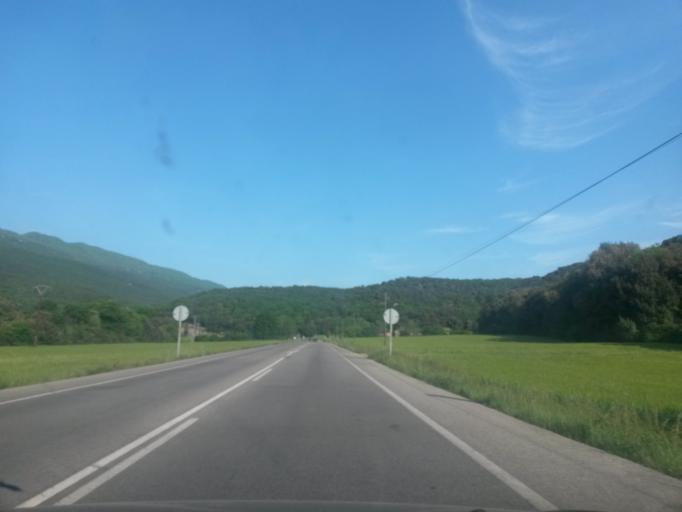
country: ES
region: Catalonia
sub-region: Provincia de Girona
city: les Planes d'Hostoles
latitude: 42.0440
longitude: 2.5625
